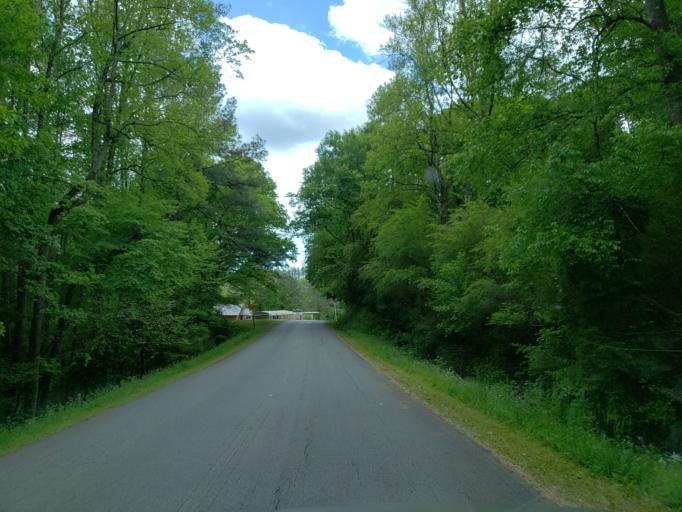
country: US
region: Georgia
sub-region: Haralson County
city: Tallapoosa
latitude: 33.7332
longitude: -85.3858
